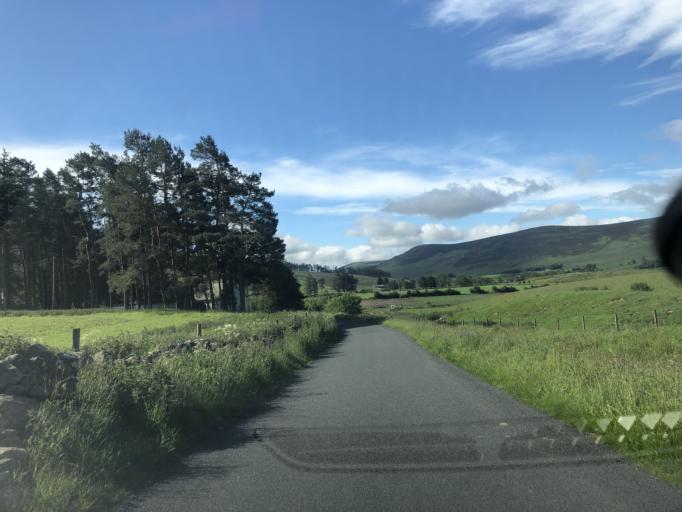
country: GB
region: Scotland
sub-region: Angus
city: Kirriemuir
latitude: 56.8157
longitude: -3.0335
